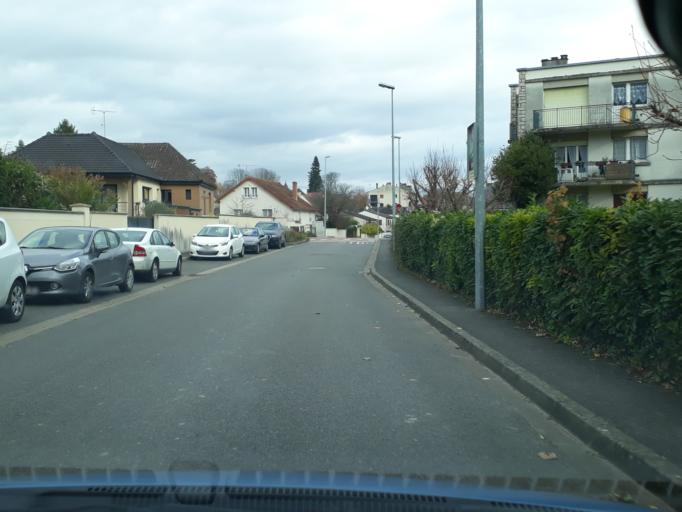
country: FR
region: Ile-de-France
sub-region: Departement de Seine-et-Marne
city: Veneux-les-Sablons
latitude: 48.3805
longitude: 2.7874
